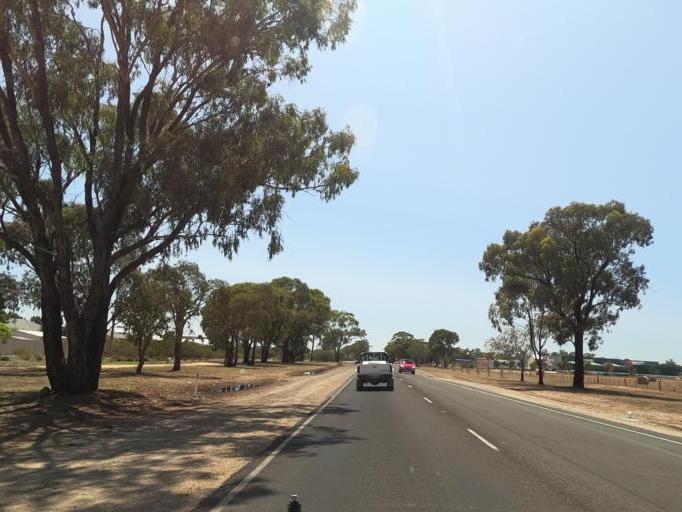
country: AU
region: Victoria
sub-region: Moira
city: Yarrawonga
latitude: -36.0124
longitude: 146.0218
